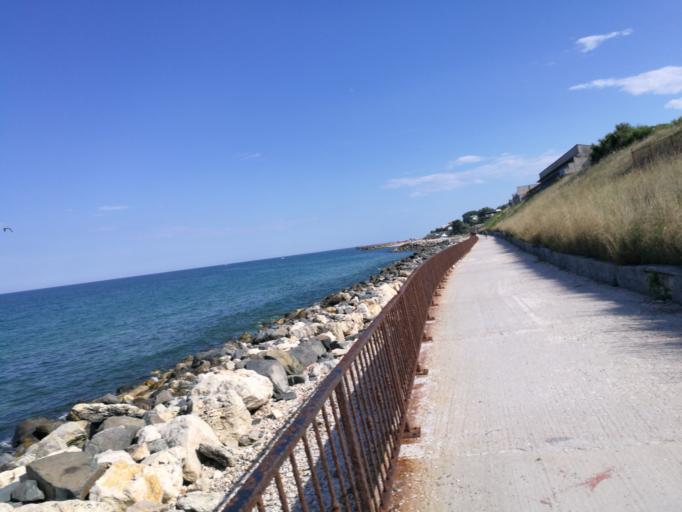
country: RO
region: Constanta
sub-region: Oras Eforie
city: Eforie
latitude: 44.0427
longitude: 28.6478
